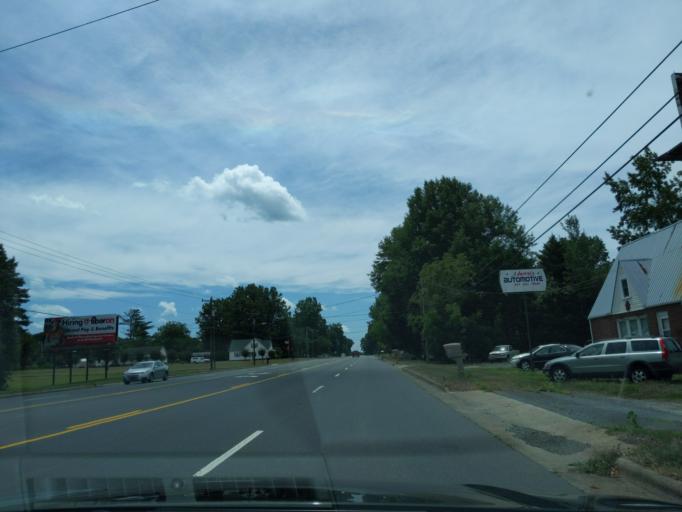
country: US
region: North Carolina
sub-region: Stanly County
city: Albemarle
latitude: 35.4235
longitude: -80.2115
